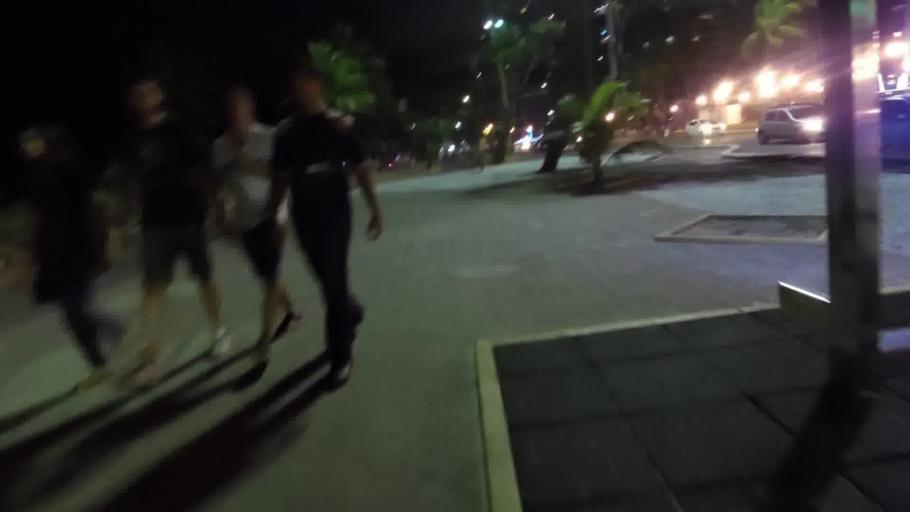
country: BR
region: Pernambuco
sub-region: Recife
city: Recife
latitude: -8.1049
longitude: -34.8866
